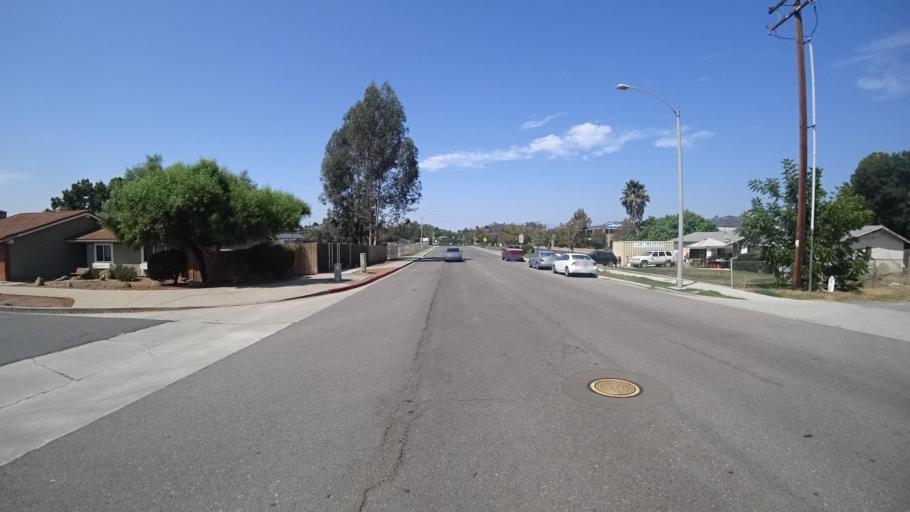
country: US
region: California
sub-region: San Diego County
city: Escondido
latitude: 33.1541
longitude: -117.0892
